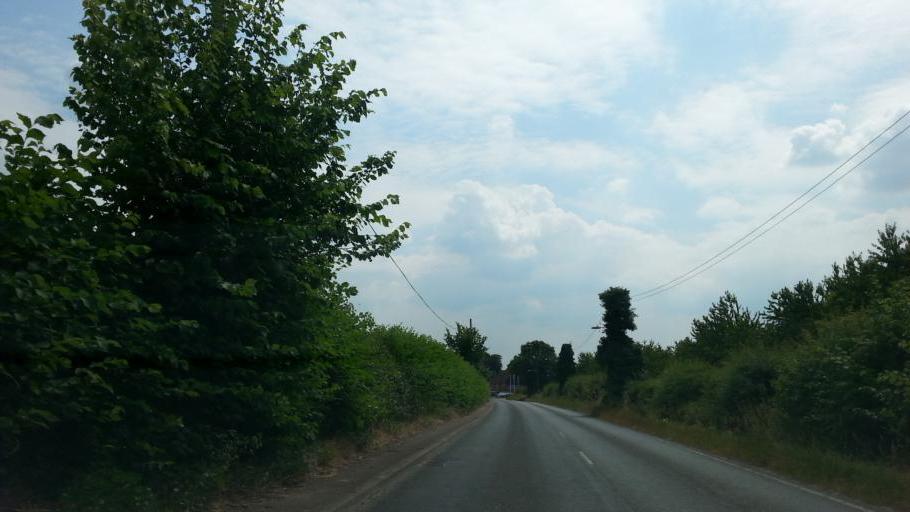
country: GB
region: England
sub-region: Suffolk
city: Lakenheath
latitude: 52.3792
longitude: 0.5268
